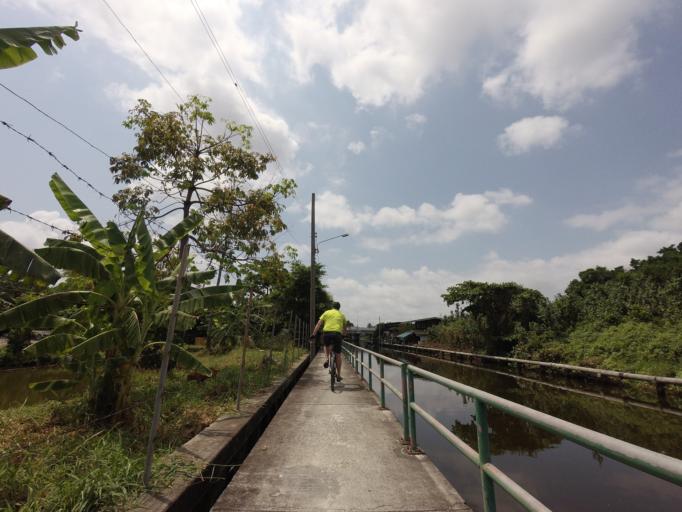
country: TH
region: Bangkok
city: Thung Khru
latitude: 13.6267
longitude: 100.4734
